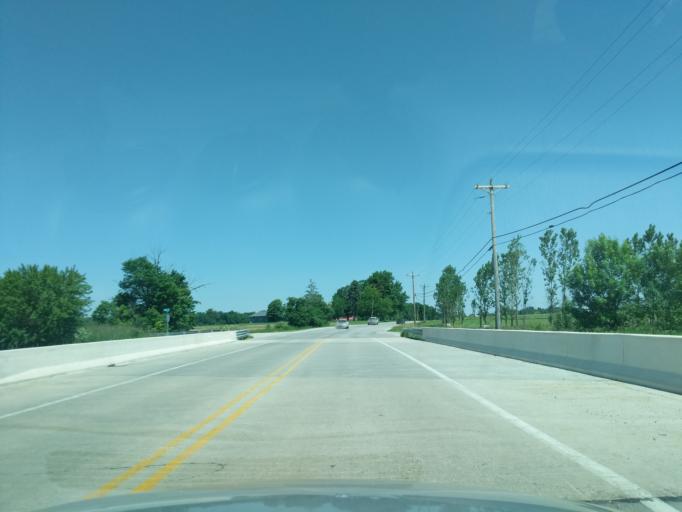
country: US
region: Indiana
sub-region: Whitley County
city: Columbia City
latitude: 41.0890
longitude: -85.4706
